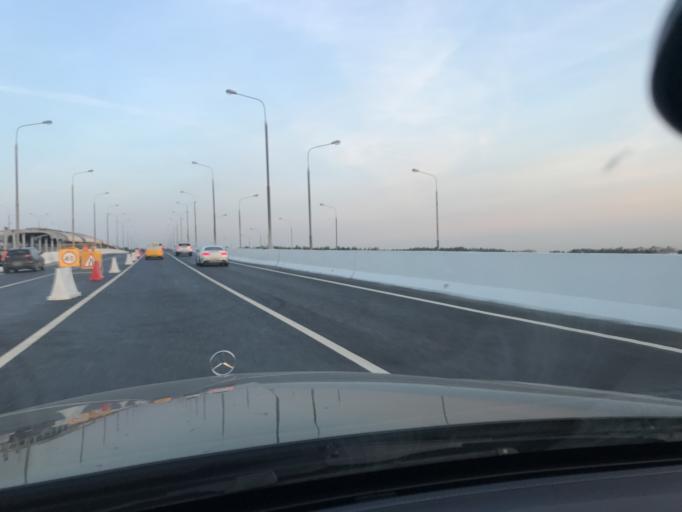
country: RU
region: Moskovskaya
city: Mosrentgen
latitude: 55.5854
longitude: 37.4357
